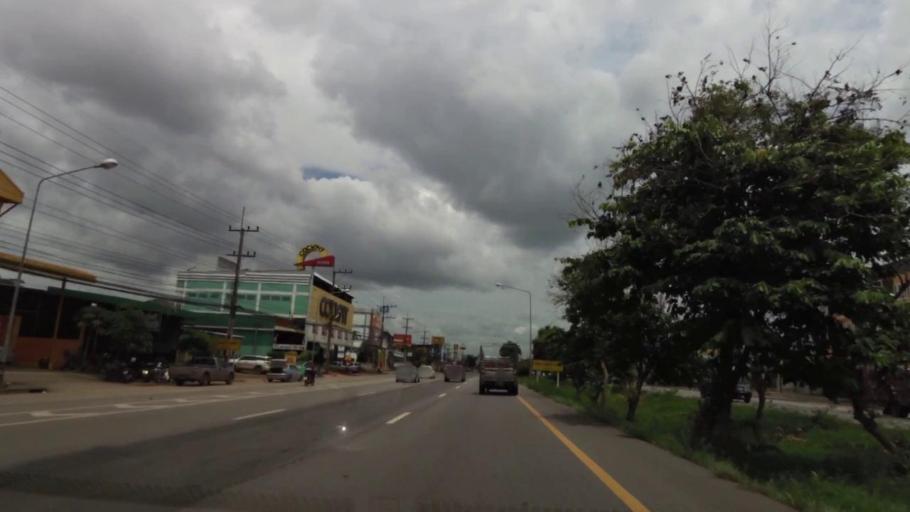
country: TH
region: Rayong
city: Klaeng
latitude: 12.7865
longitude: 101.6680
